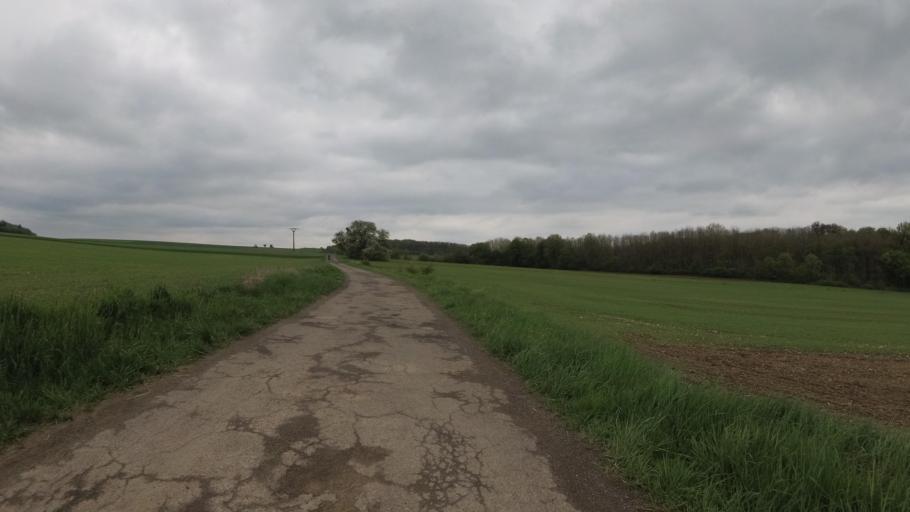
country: DE
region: Saarland
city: Merzig
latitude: 49.4061
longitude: 6.5596
